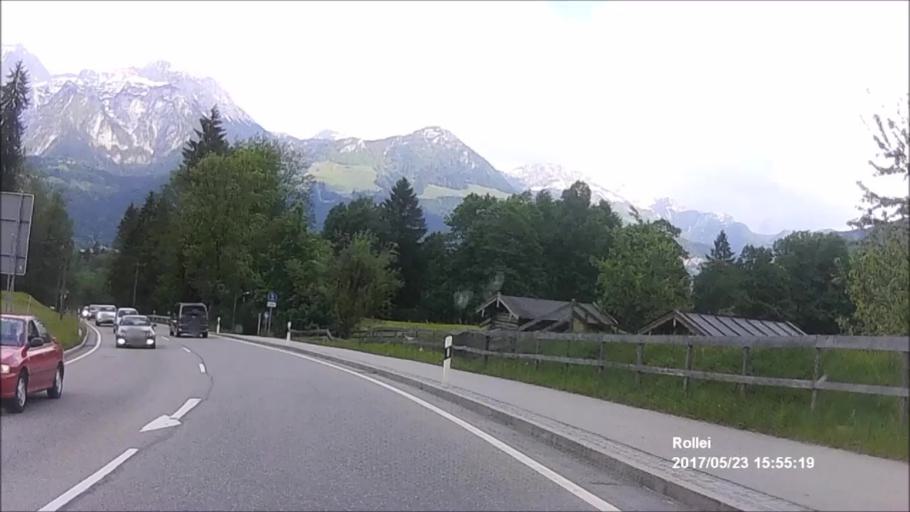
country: DE
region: Bavaria
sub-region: Upper Bavaria
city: Schoenau am Koenigssee
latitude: 47.6209
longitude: 12.9661
